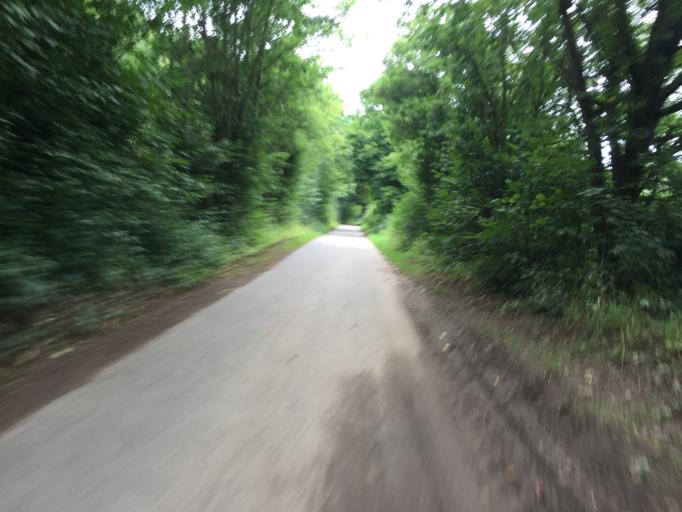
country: DE
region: Hesse
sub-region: Regierungsbezirk Kassel
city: Bad Hersfeld
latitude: 50.8822
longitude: 9.7432
